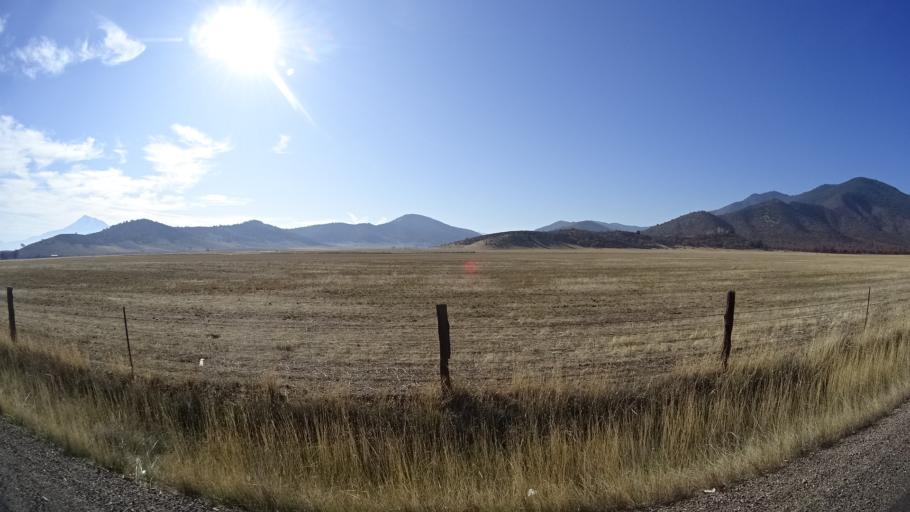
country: US
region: California
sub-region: Siskiyou County
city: Montague
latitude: 41.6548
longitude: -122.5691
